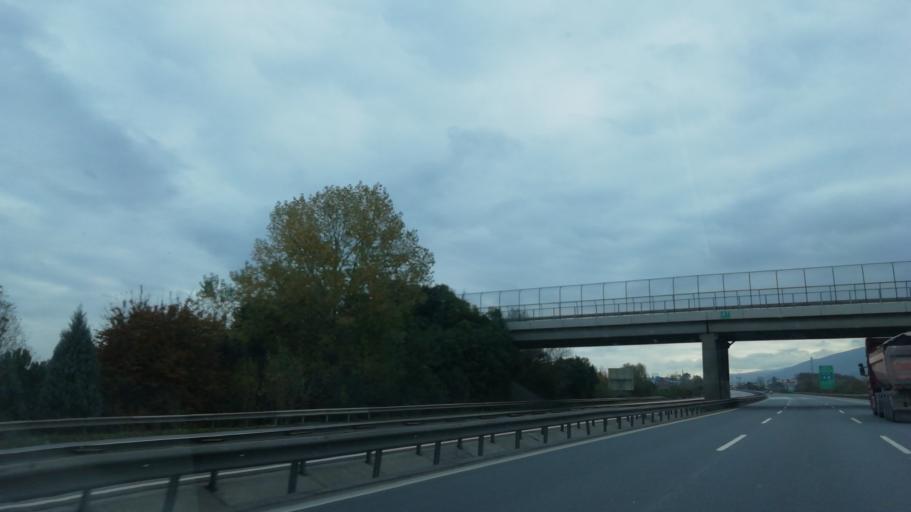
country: TR
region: Kocaeli
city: Derbent
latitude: 40.7316
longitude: 30.0575
